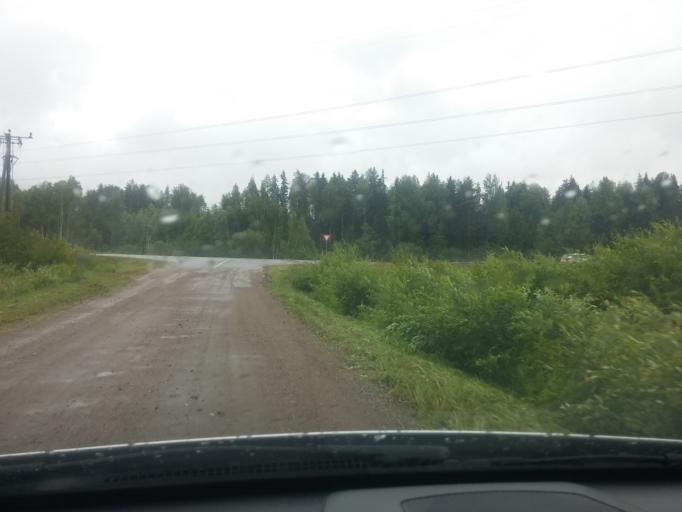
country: LV
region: Ogre
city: Ogre
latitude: 56.8598
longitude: 24.5816
